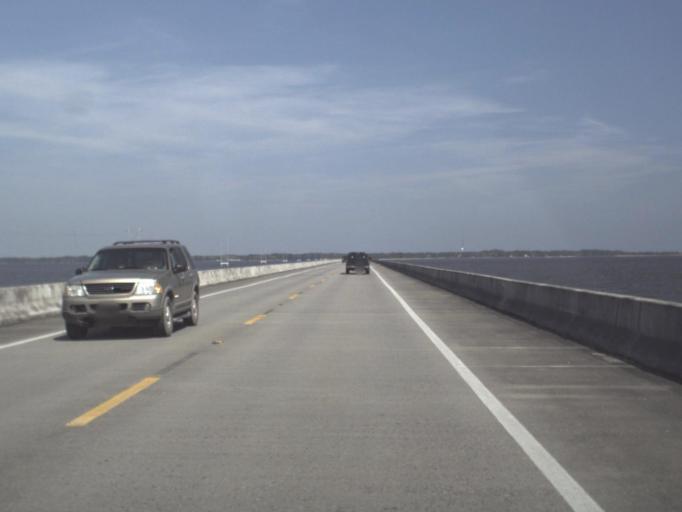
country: US
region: Florida
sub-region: Franklin County
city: Apalachicola
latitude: 29.7306
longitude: -84.9365
